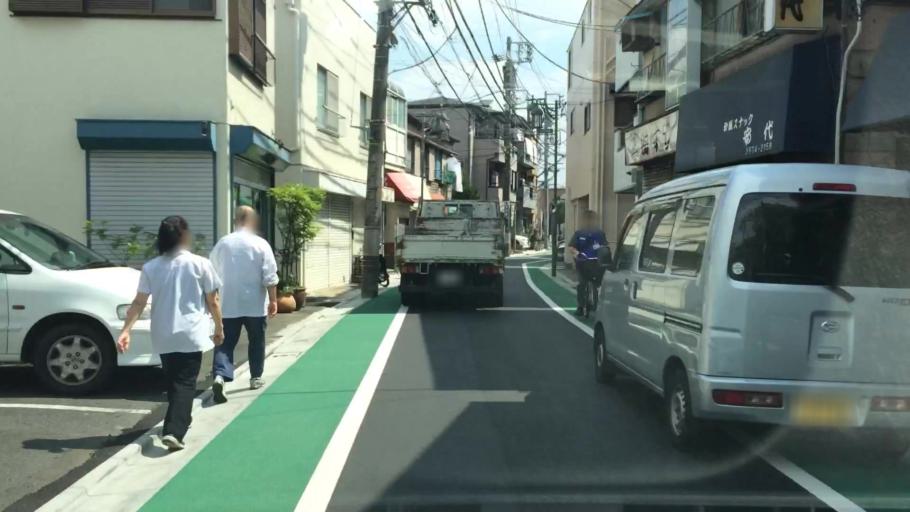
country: JP
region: Tokyo
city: Tokyo
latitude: 35.7464
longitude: 139.6891
